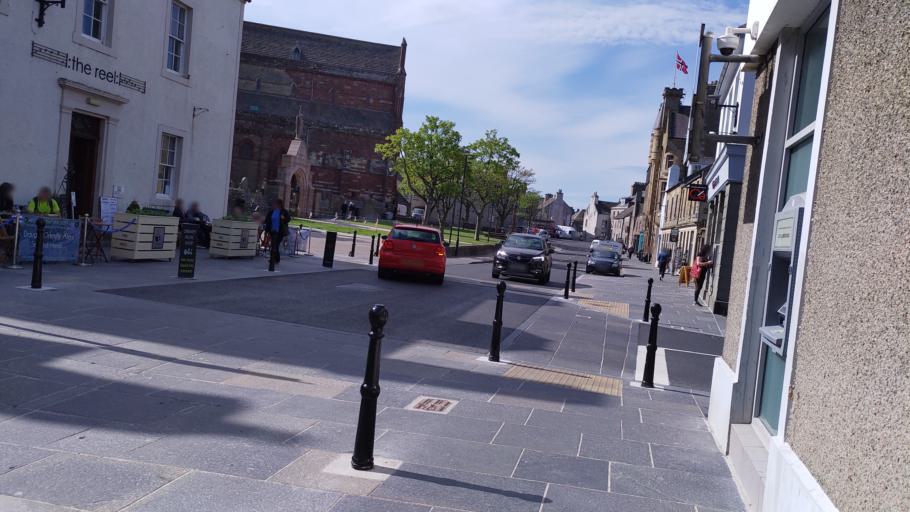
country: GB
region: Scotland
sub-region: Orkney Islands
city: Orkney
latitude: 58.9823
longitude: -2.9598
